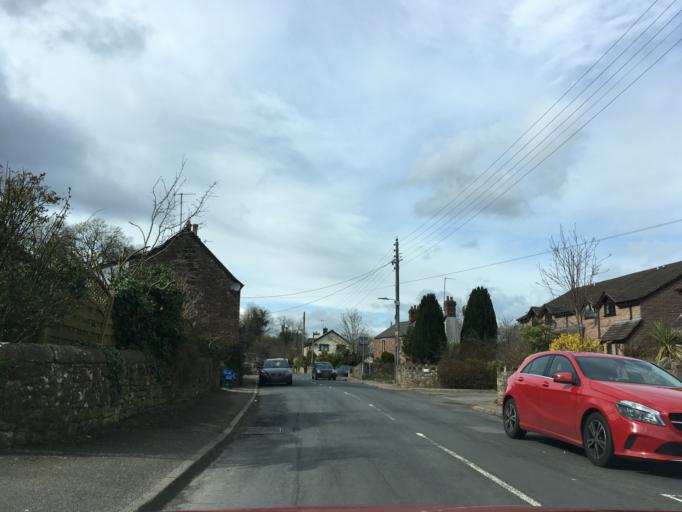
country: GB
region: England
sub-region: Gloucestershire
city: Coleford
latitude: 51.7699
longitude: -2.6223
